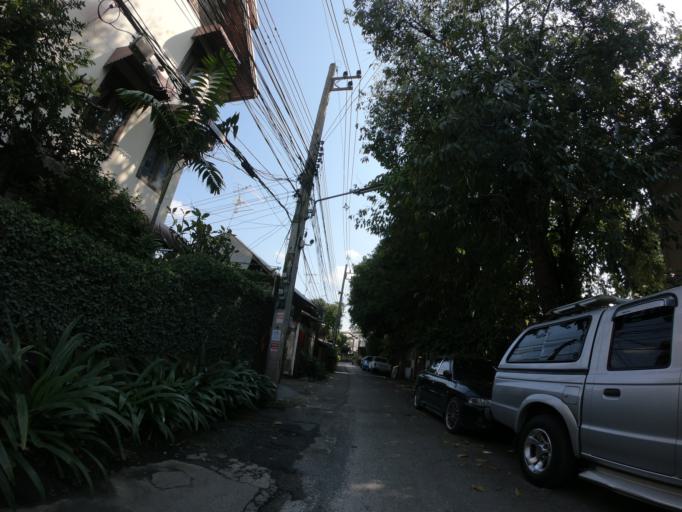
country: TH
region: Chiang Mai
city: Chiang Mai
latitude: 18.7885
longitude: 99.0069
